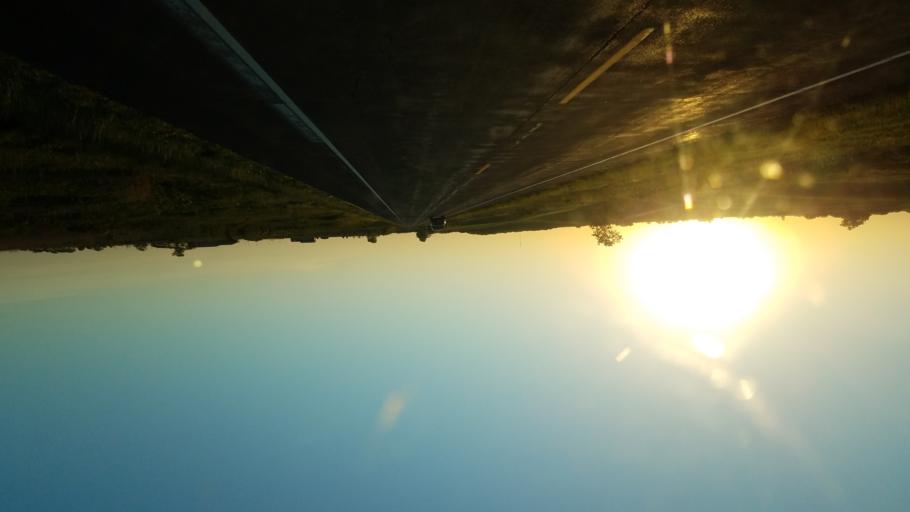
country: US
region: Missouri
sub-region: Schuyler County
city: Lancaster
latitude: 40.4927
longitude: -92.5672
